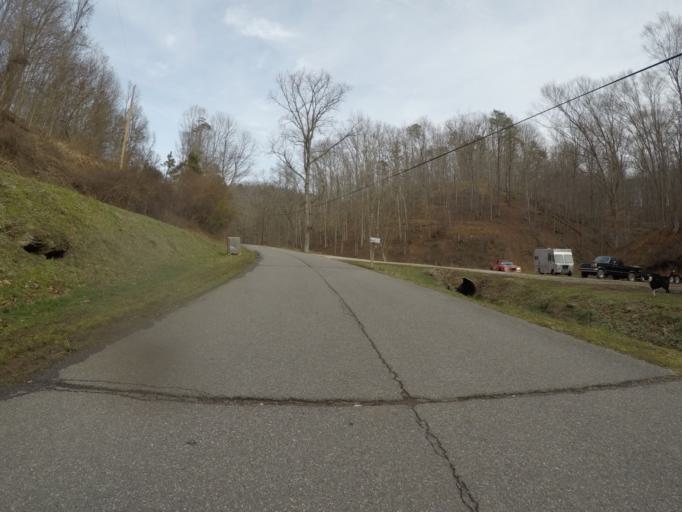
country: US
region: West Virginia
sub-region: Wayne County
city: Lavalette
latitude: 38.3388
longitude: -82.3762
